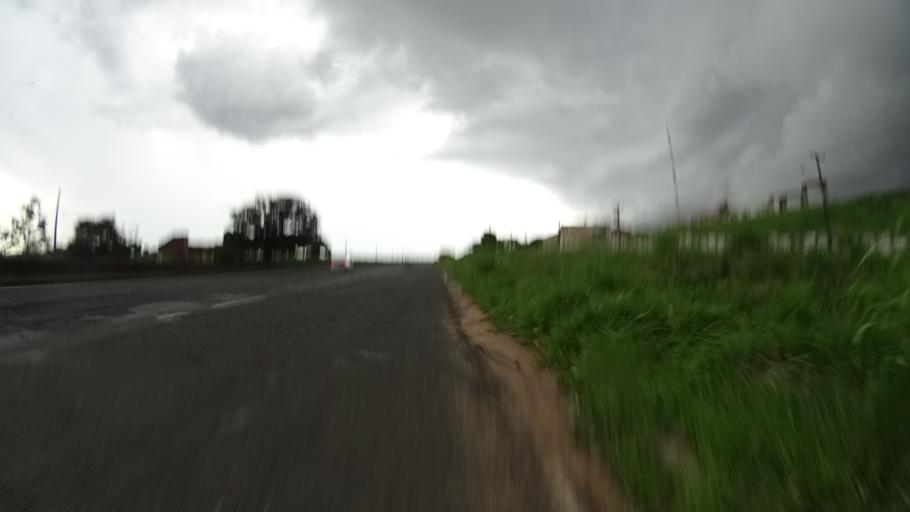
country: BR
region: Sao Paulo
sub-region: Marilia
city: Marilia
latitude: -22.2235
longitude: -49.8851
